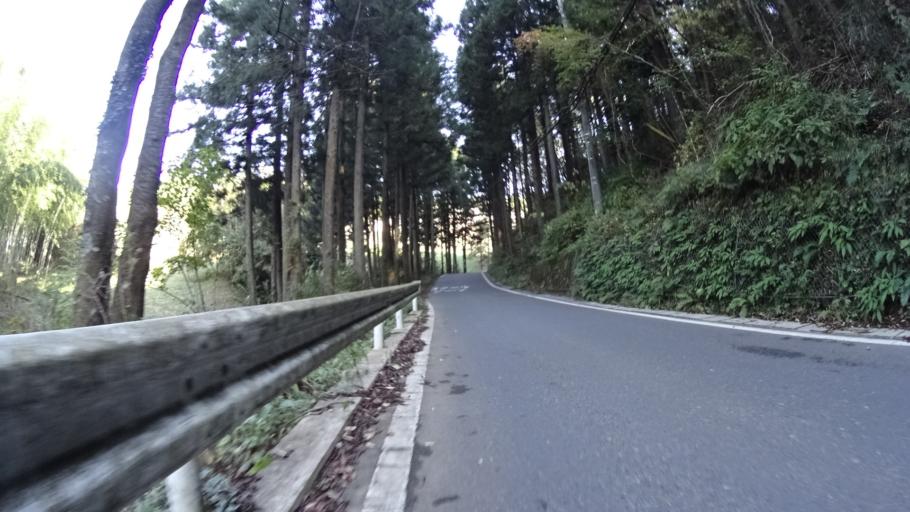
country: JP
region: Yamanashi
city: Uenohara
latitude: 35.6409
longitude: 139.1292
